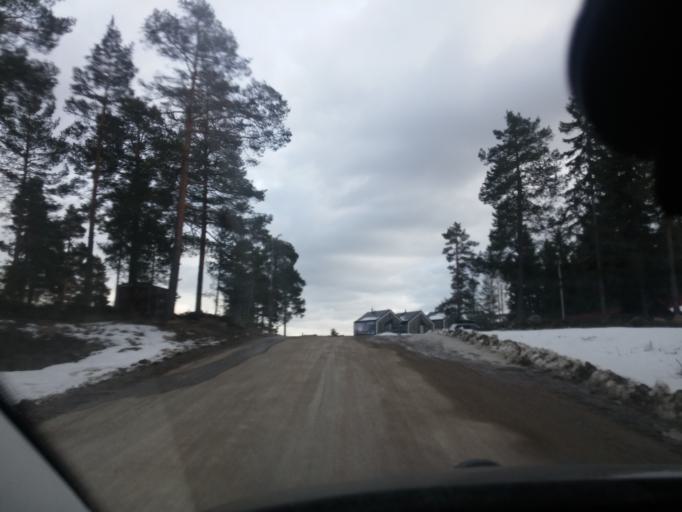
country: SE
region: Gaevleborg
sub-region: Ljusdals Kommun
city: Jaervsoe
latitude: 61.7192
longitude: 16.1576
